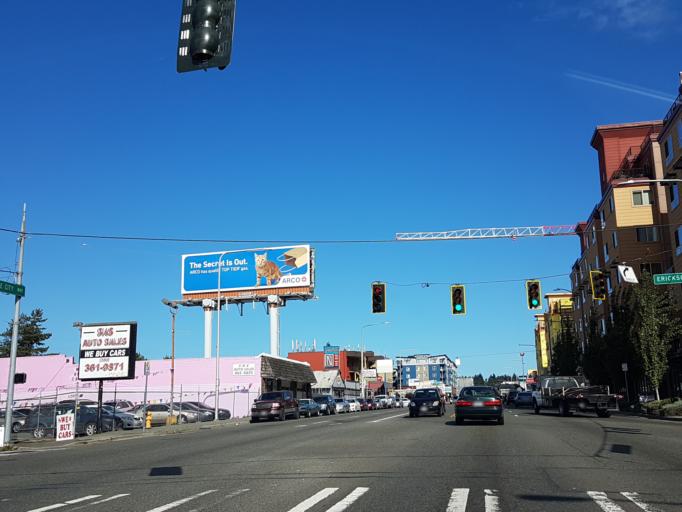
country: US
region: Washington
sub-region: King County
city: Lake Forest Park
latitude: 47.7281
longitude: -122.2922
